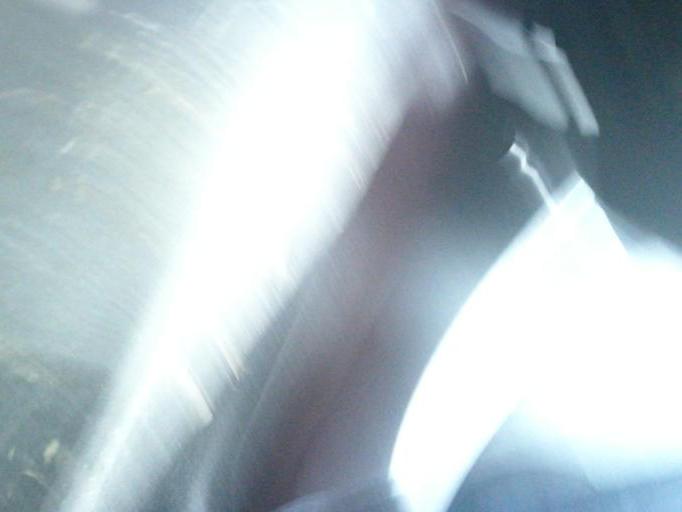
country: FR
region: Brittany
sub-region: Departement d'Ille-et-Vilaine
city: Bedee
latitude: 48.1707
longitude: -1.9558
